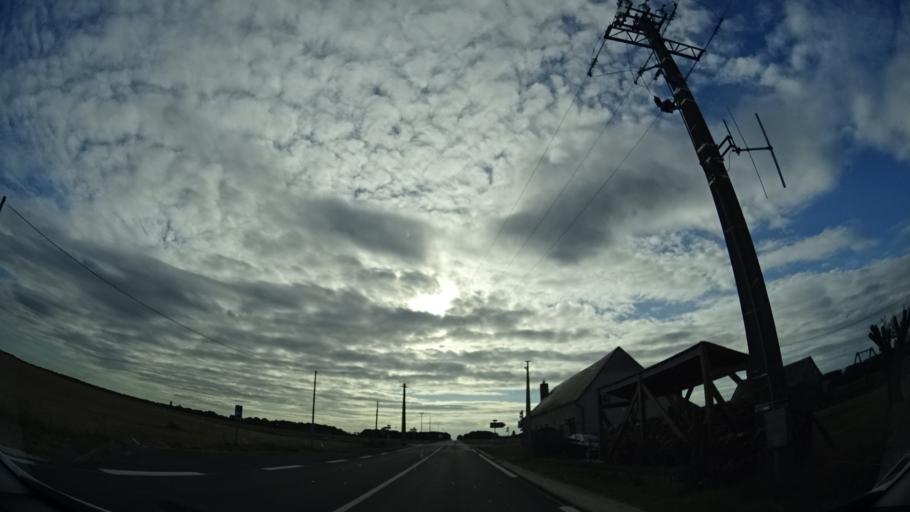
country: FR
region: Centre
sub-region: Departement du Loir-et-Cher
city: La Ville-aux-Clercs
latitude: 47.8923
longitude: 1.0837
